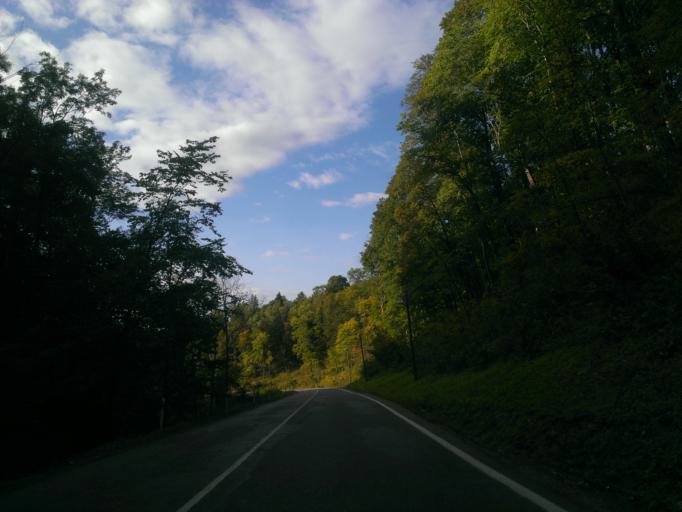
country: LV
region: Sigulda
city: Sigulda
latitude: 57.1646
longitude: 24.8493
